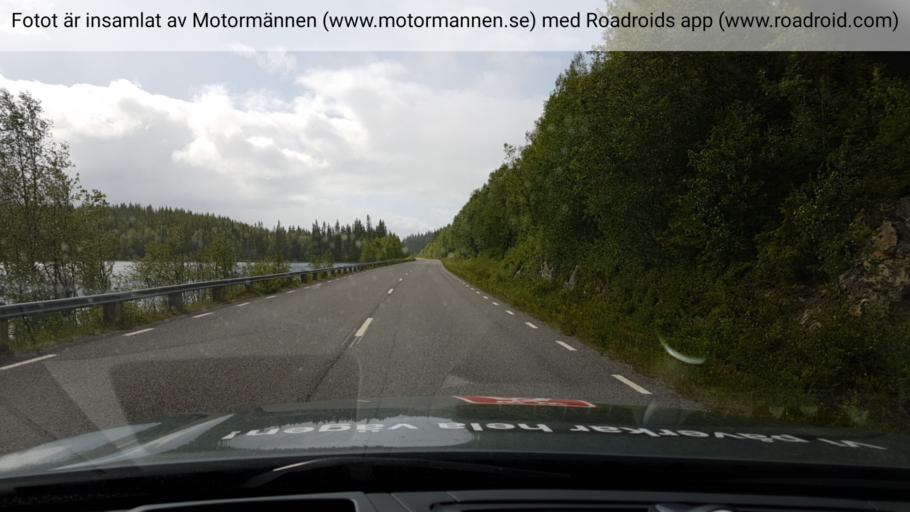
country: SE
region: Jaemtland
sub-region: Are Kommun
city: Are
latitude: 63.6807
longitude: 13.0309
